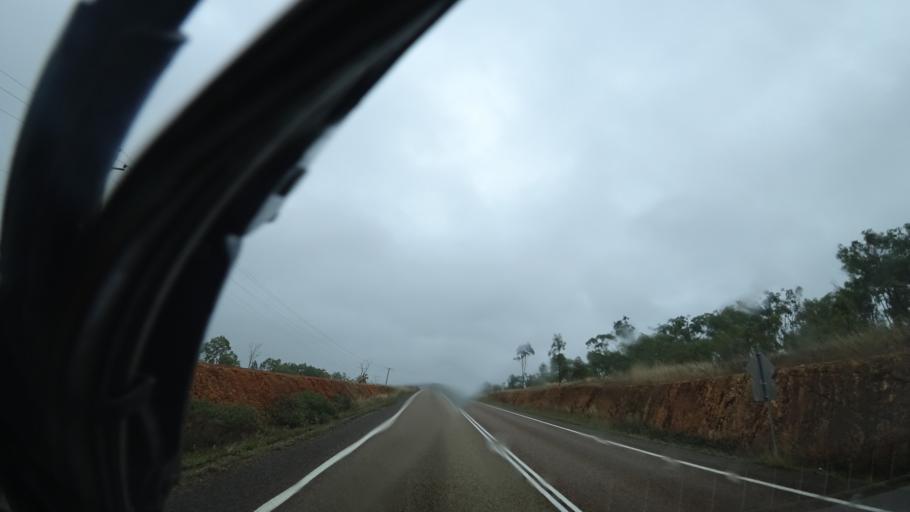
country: AU
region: Queensland
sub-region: Tablelands
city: Ravenshoe
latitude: -17.6985
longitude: 145.2055
